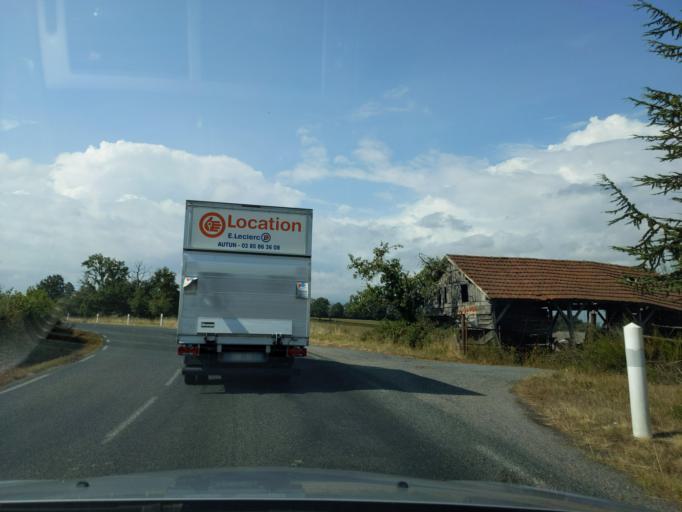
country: FR
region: Bourgogne
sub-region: Departement de Saone-et-Loire
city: Bourbon-Lancy
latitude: 46.6454
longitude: 3.7788
